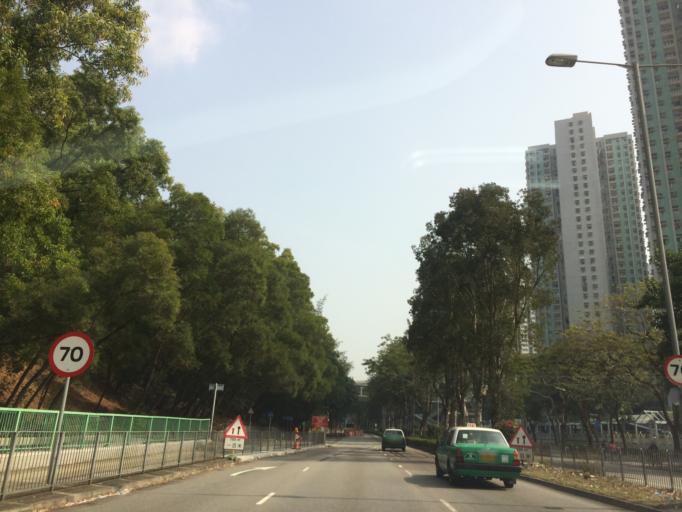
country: HK
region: Tai Po
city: Tai Po
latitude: 22.4560
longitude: 114.1724
